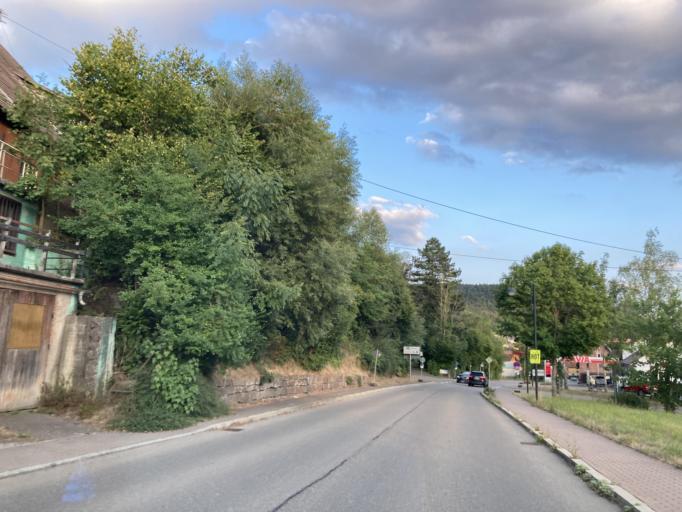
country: DE
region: Baden-Wuerttemberg
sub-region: Karlsruhe Region
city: Glatten
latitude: 48.4471
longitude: 8.5097
